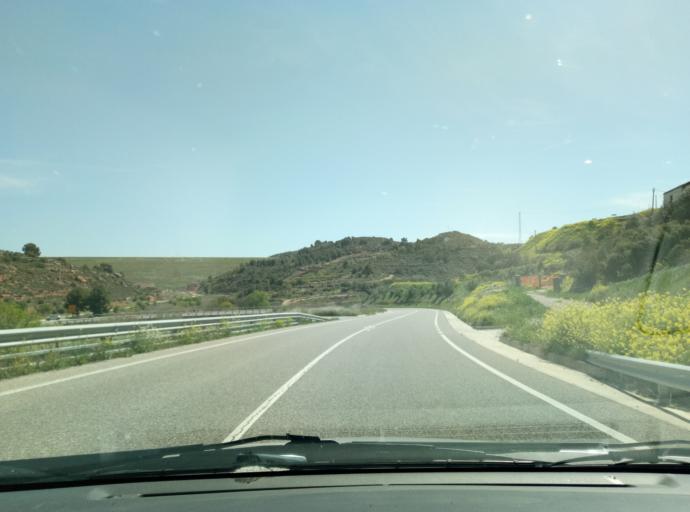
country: ES
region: Catalonia
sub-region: Provincia de Lleida
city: el Cogul
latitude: 41.4517
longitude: 0.7443
